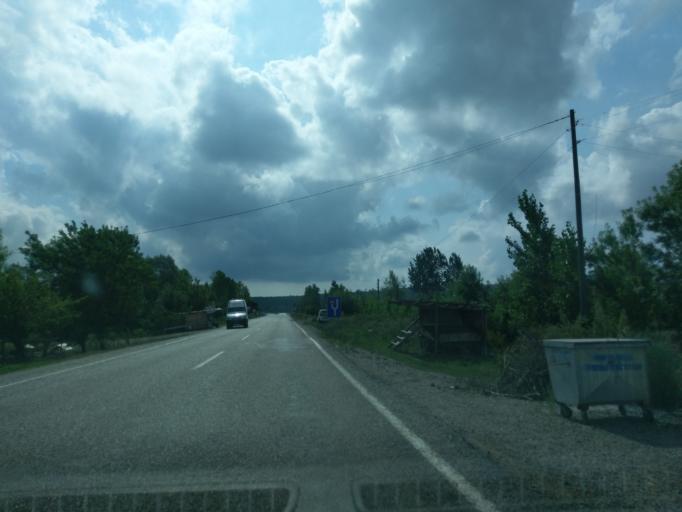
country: TR
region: Sinop
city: Sinop
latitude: 42.0154
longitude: 35.0540
